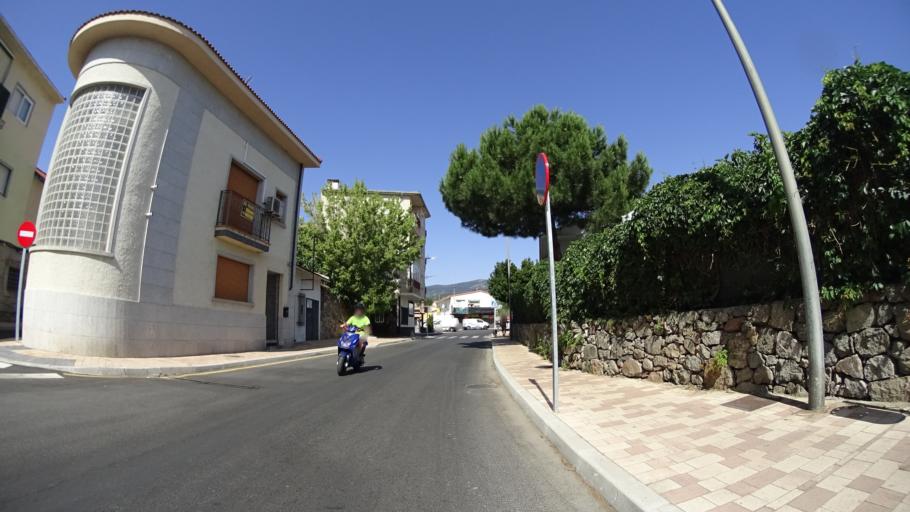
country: ES
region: Madrid
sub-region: Provincia de Madrid
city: Guadarrama
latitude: 40.6748
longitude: -4.0886
